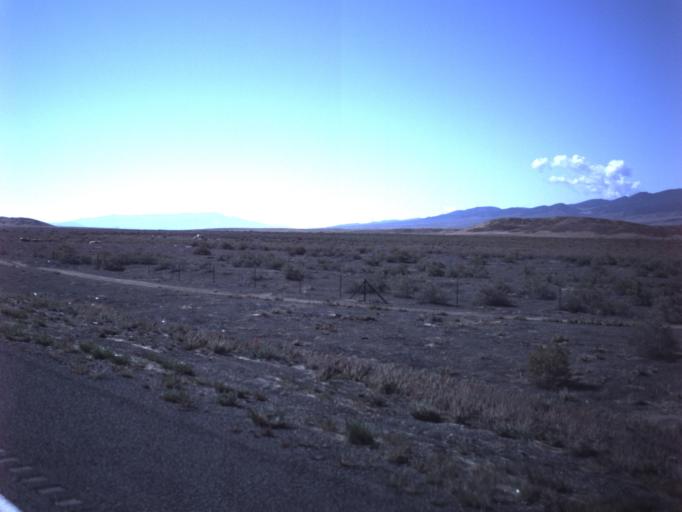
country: US
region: Utah
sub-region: Sanpete County
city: Gunnison
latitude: 39.1865
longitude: -111.8413
